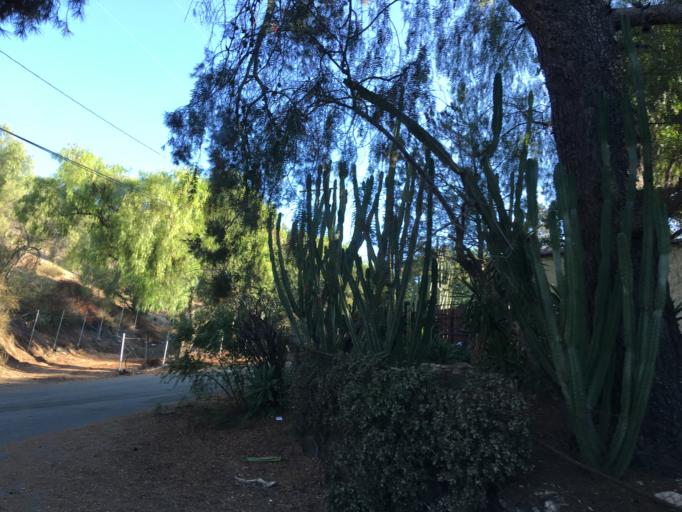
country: US
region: California
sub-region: Los Angeles County
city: San Fernando
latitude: 34.2871
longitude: -118.3777
